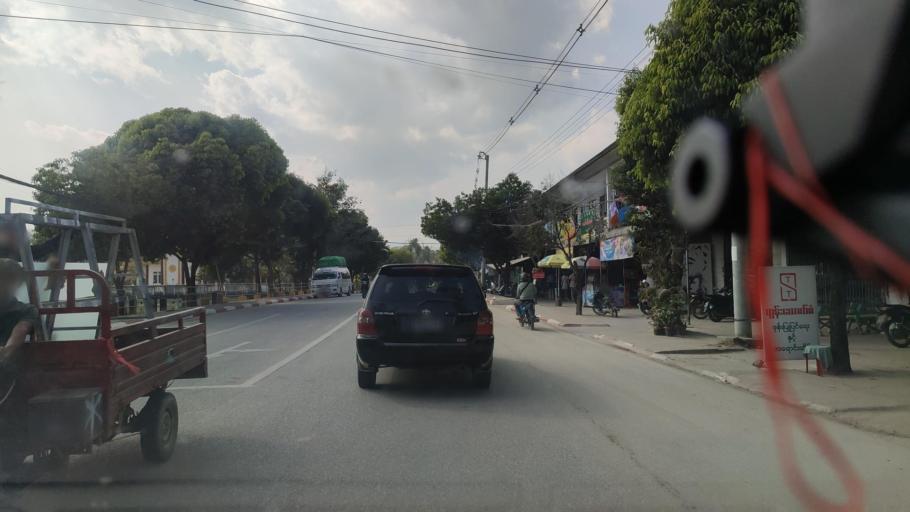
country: TH
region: Chiang Rai
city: Mae Sai
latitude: 21.2974
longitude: 99.6134
